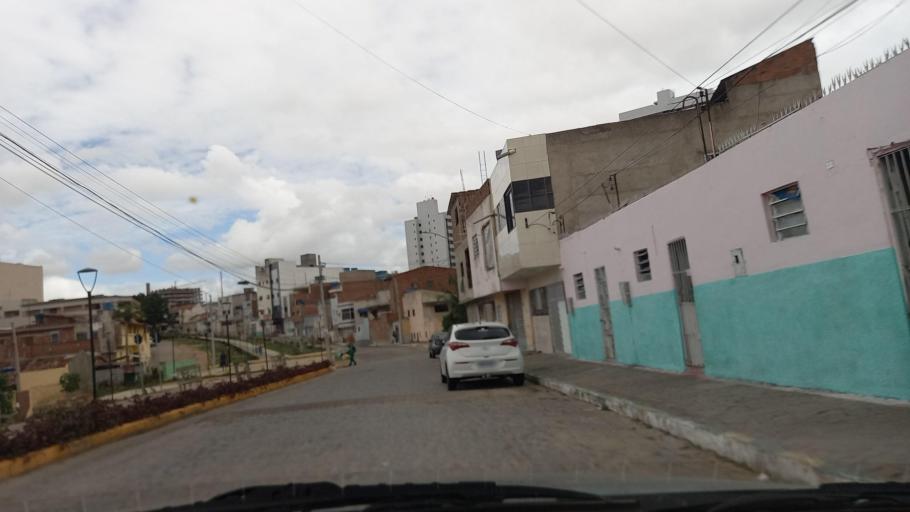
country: BR
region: Pernambuco
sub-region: Caruaru
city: Caruaru
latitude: -8.2796
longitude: -35.9650
